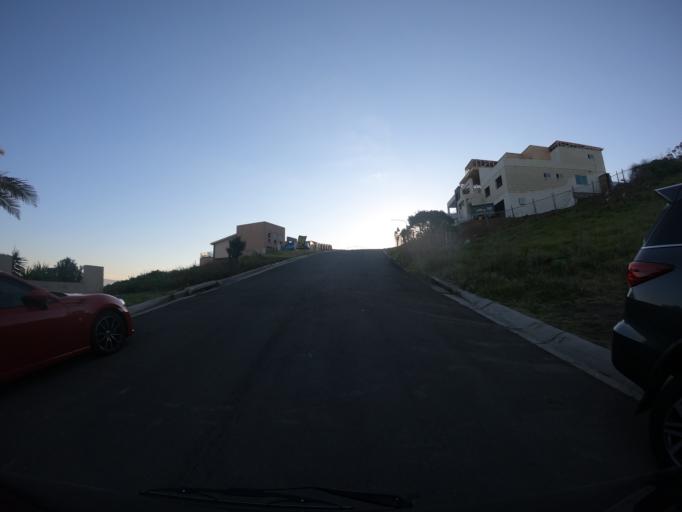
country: AU
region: New South Wales
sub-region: Wollongong
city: Lake Heights
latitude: -34.4771
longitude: 150.8639
